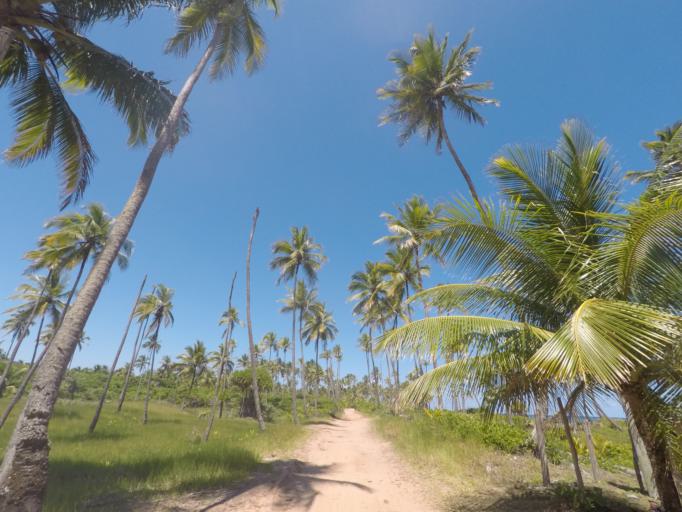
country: BR
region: Bahia
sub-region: Marau
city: Marau
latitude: -14.0172
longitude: -38.9451
